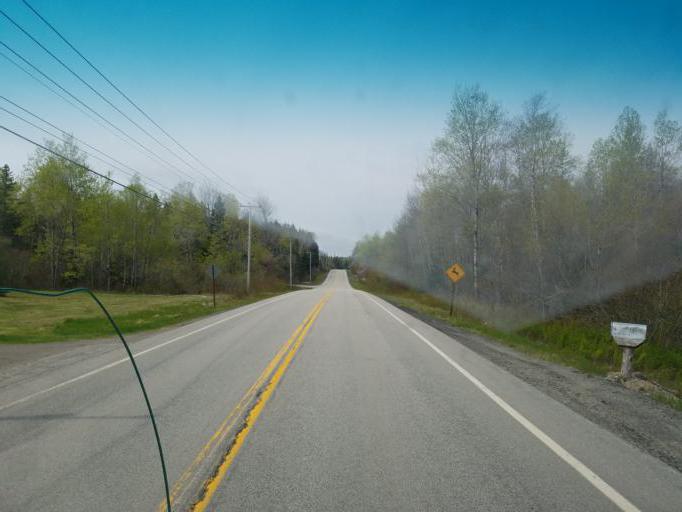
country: US
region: Maine
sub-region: Washington County
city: Eastport
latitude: 44.7941
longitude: -67.1535
